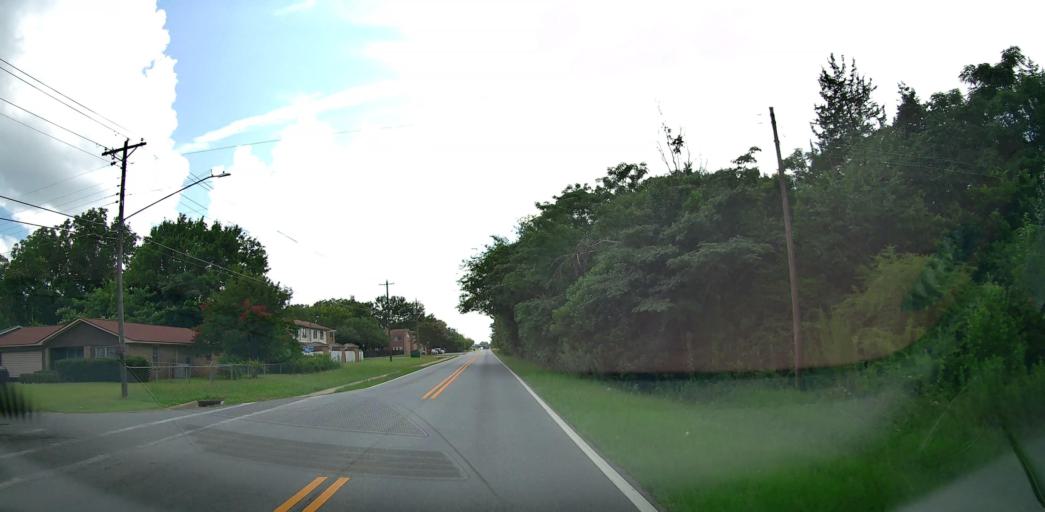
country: US
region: Georgia
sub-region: Houston County
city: Warner Robins
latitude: 32.6330
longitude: -83.6364
